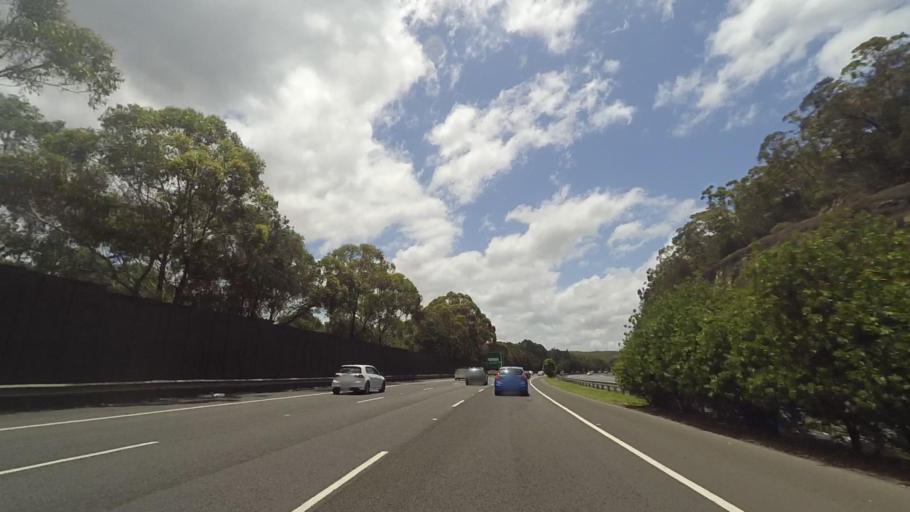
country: AU
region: New South Wales
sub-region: Ku-ring-gai
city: North Wahroonga
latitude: -33.7011
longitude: 151.1180
